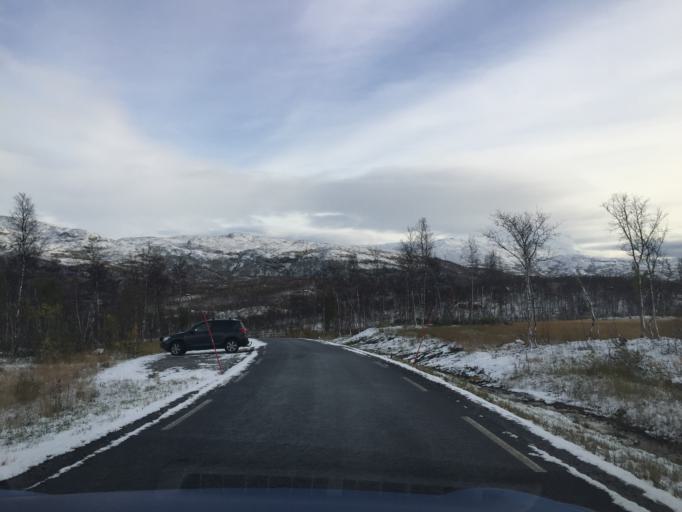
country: NO
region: Nordland
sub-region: Sorfold
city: Straumen
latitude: 67.0857
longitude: 16.0241
